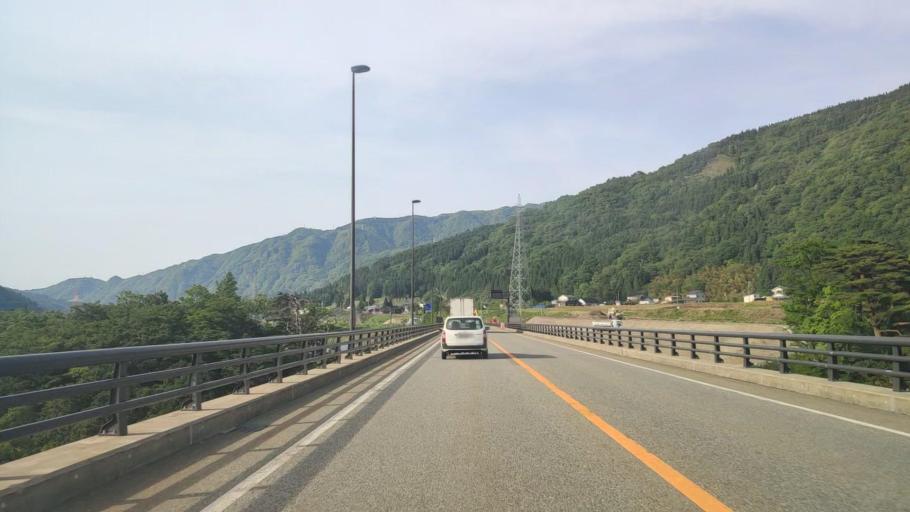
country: JP
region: Toyama
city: Yatsuomachi-higashikumisaka
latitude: 36.5156
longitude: 137.2295
